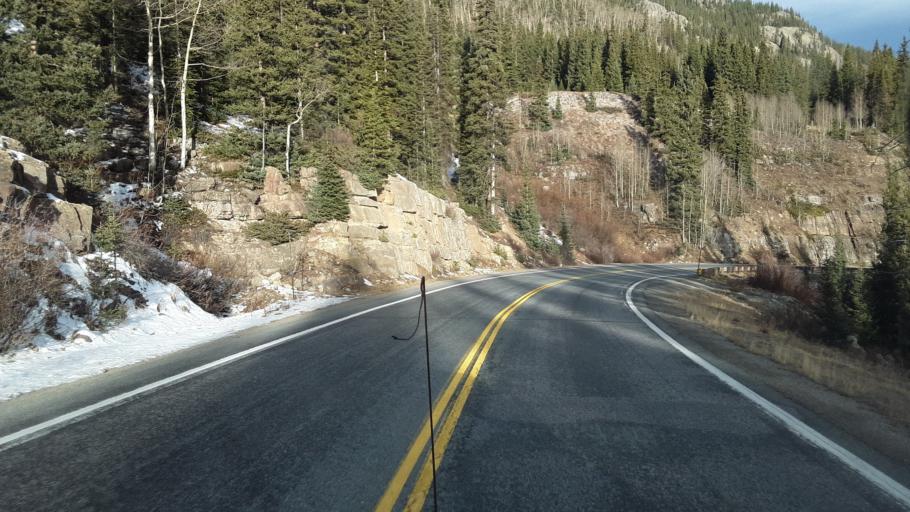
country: US
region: Colorado
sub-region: San Juan County
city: Silverton
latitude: 37.7793
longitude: -107.6721
